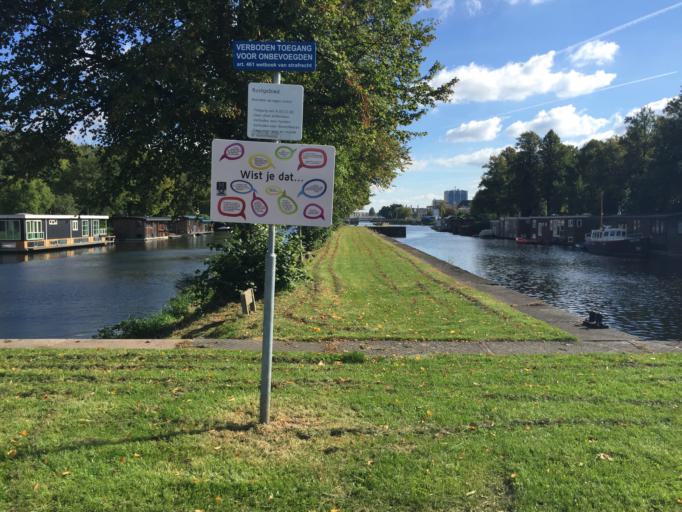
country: NL
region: Utrecht
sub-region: Gemeente Utrecht
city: Utrecht
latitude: 52.0891
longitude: 5.0913
